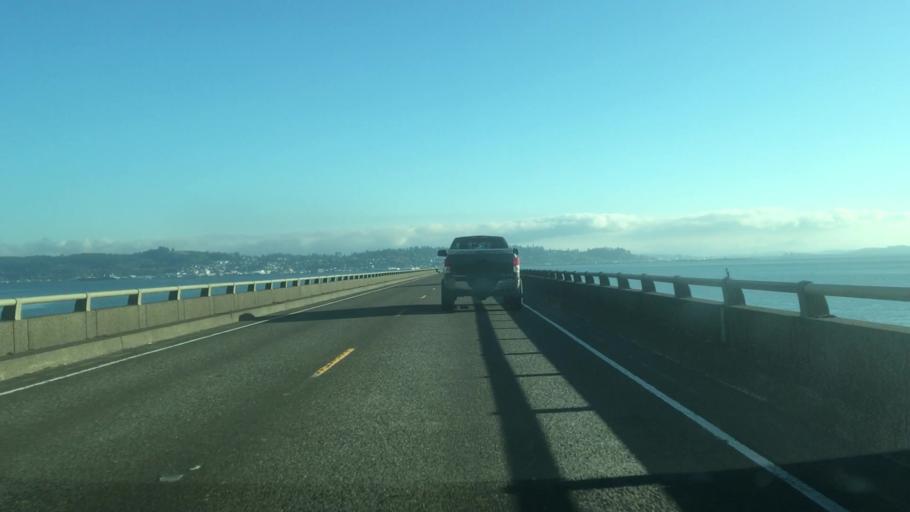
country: US
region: Oregon
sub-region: Clatsop County
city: Astoria
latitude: 46.2277
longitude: -123.8685
